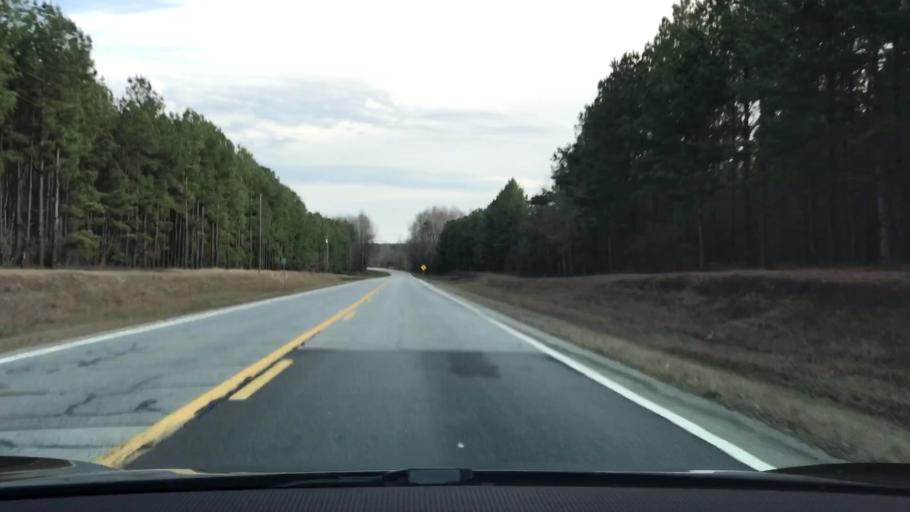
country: US
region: Georgia
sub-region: Glascock County
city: Gibson
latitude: 33.3379
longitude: -82.5714
